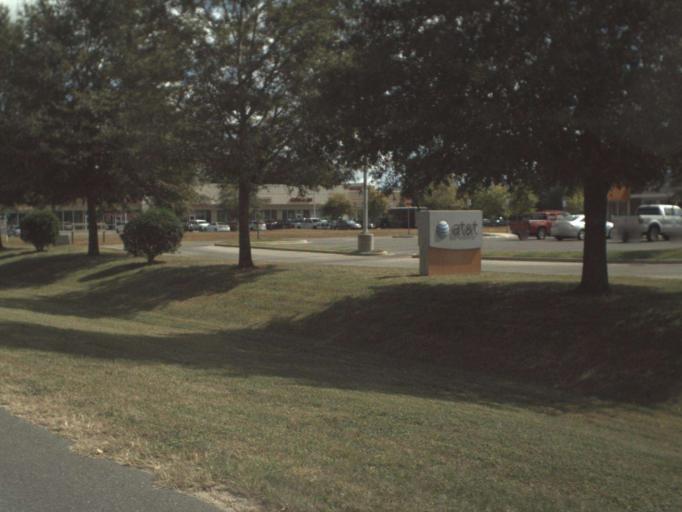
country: US
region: Florida
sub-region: Santa Rosa County
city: Pace
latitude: 30.6034
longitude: -87.1253
